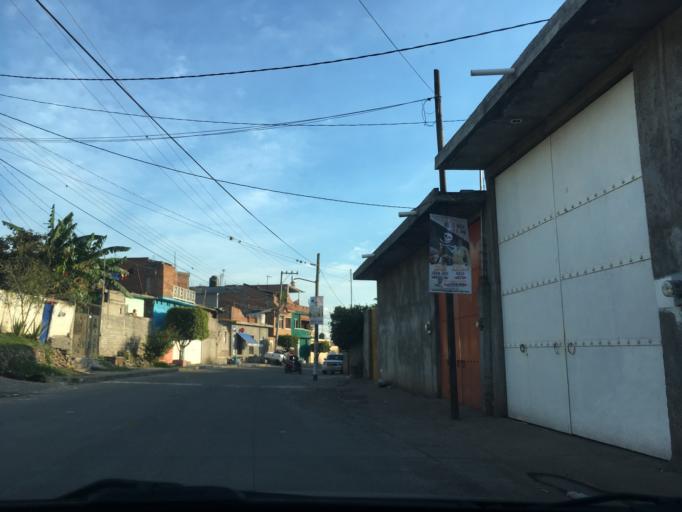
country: MX
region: Michoacan
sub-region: Cuitzeo
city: San Juan Benito Juarez (San Juan Tararameo)
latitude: 19.8735
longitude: -101.1423
